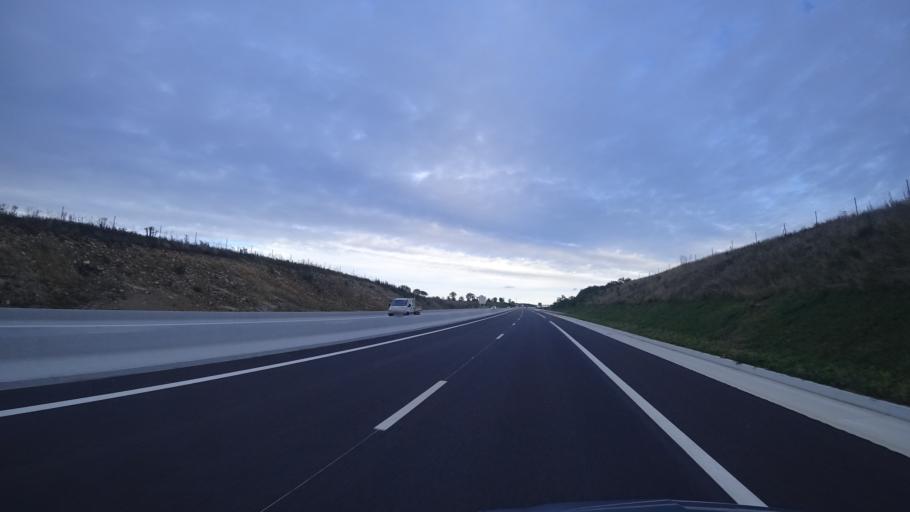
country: FR
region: Midi-Pyrenees
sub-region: Departement de l'Aveyron
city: Baraqueville
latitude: 44.2902
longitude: 2.4584
